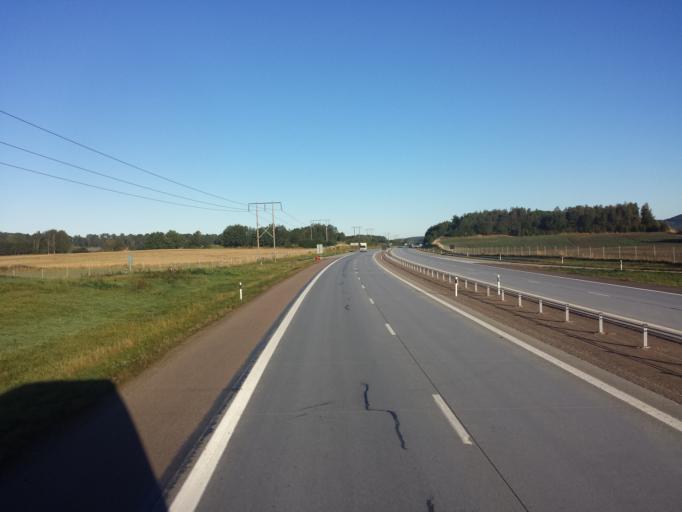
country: SE
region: Halland
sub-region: Halmstads Kommun
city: Getinge
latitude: 56.8514
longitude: 12.6771
